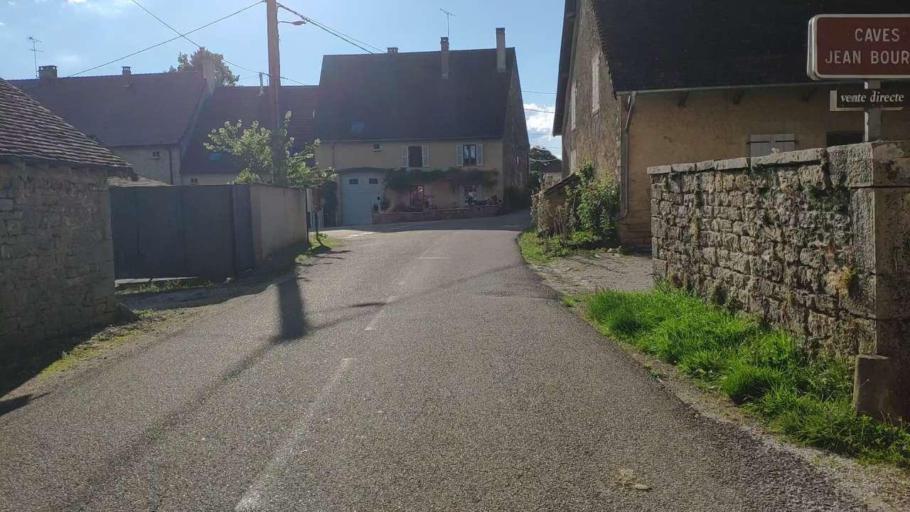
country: FR
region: Franche-Comte
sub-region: Departement du Jura
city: Bletterans
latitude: 46.7623
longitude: 5.5243
